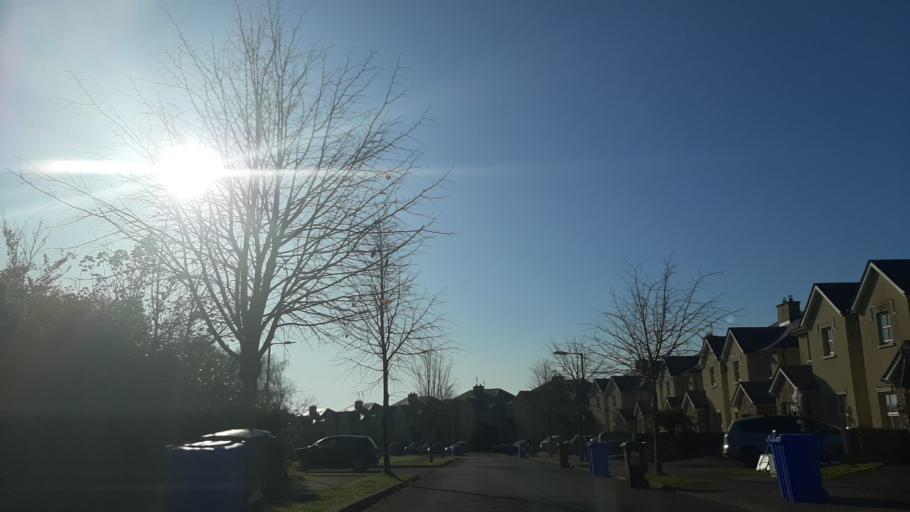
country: IE
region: Leinster
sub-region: Kildare
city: Rathangan
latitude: 53.2191
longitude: -7.0066
